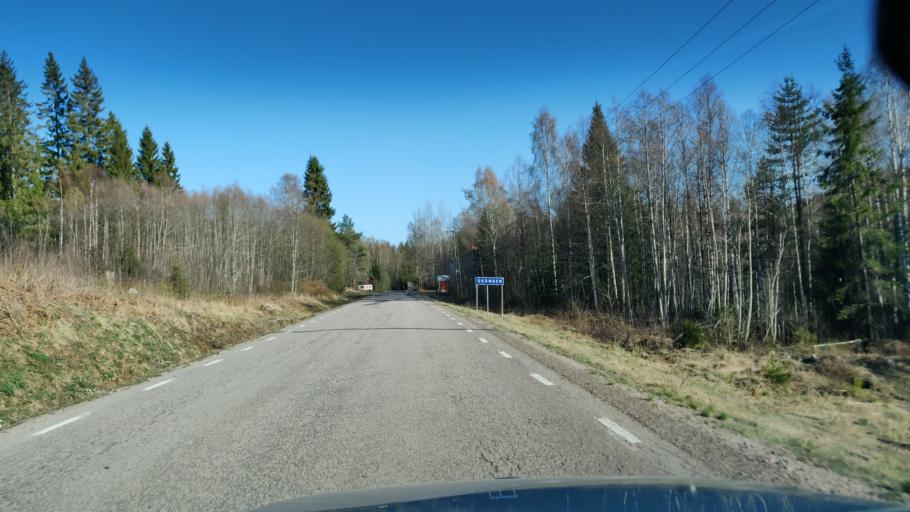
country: SE
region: Vaermland
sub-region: Munkfors Kommun
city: Munkfors
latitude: 59.9849
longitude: 13.3981
